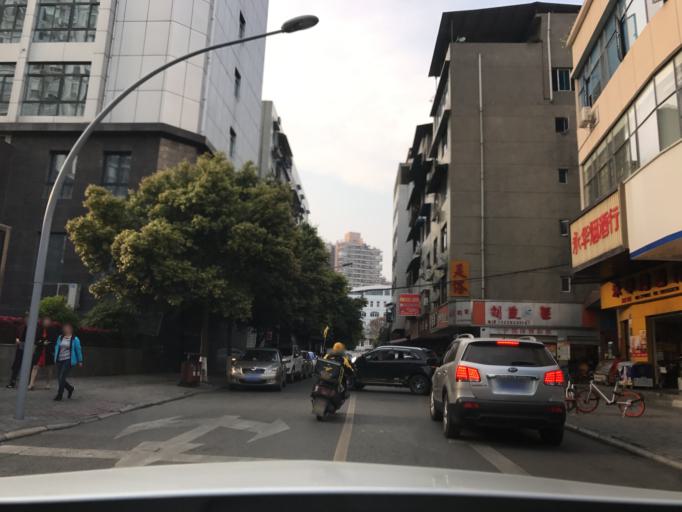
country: CN
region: Sichuan
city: Mianyang
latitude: 31.4549
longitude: 104.7495
